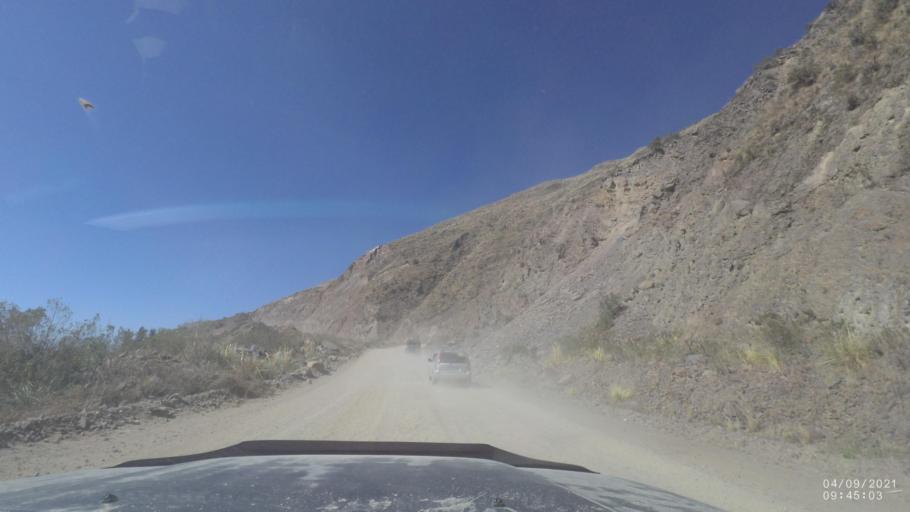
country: BO
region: Cochabamba
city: Sipe Sipe
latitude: -17.3447
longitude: -66.3902
